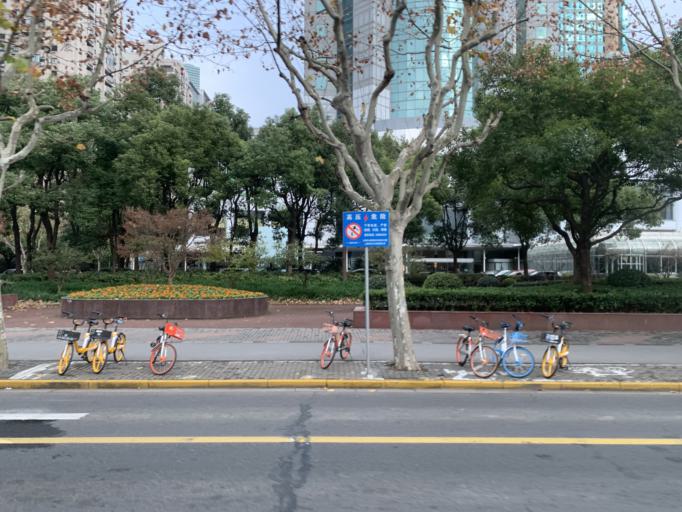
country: CN
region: Shanghai Shi
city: Pudong
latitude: 31.2250
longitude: 121.5236
